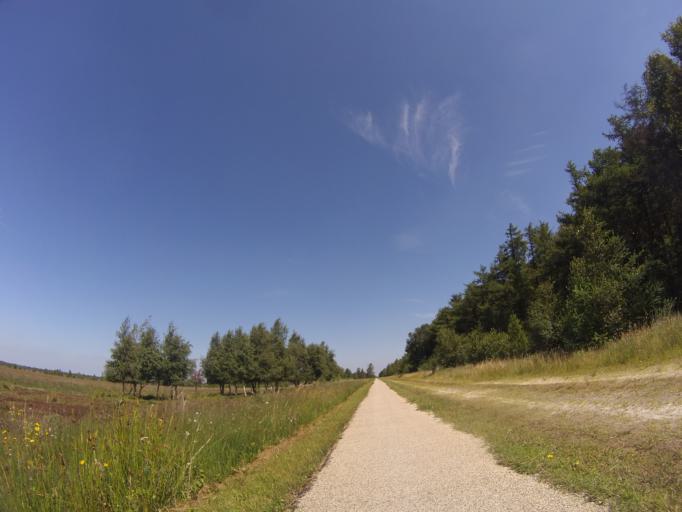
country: DE
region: Lower Saxony
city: Twist
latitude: 52.6787
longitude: 7.0587
